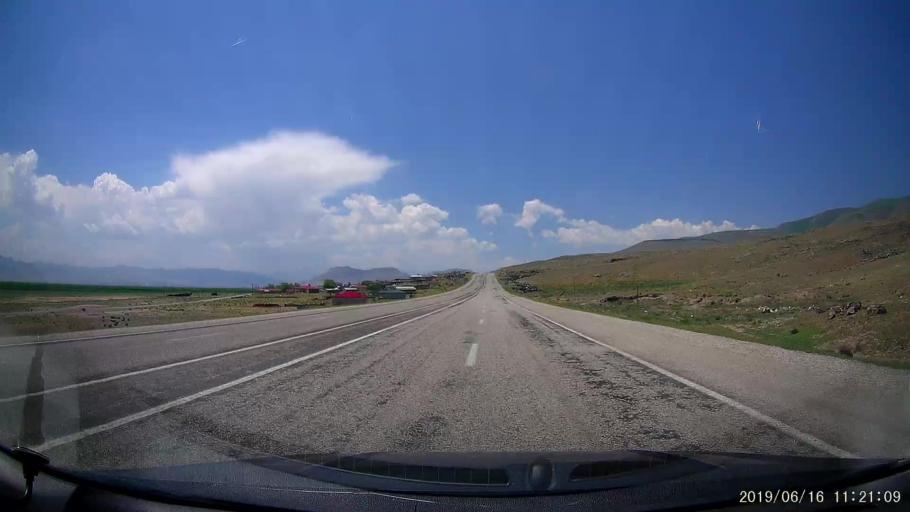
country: TR
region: Agri
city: Dogubayazit
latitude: 39.6954
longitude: 44.0756
